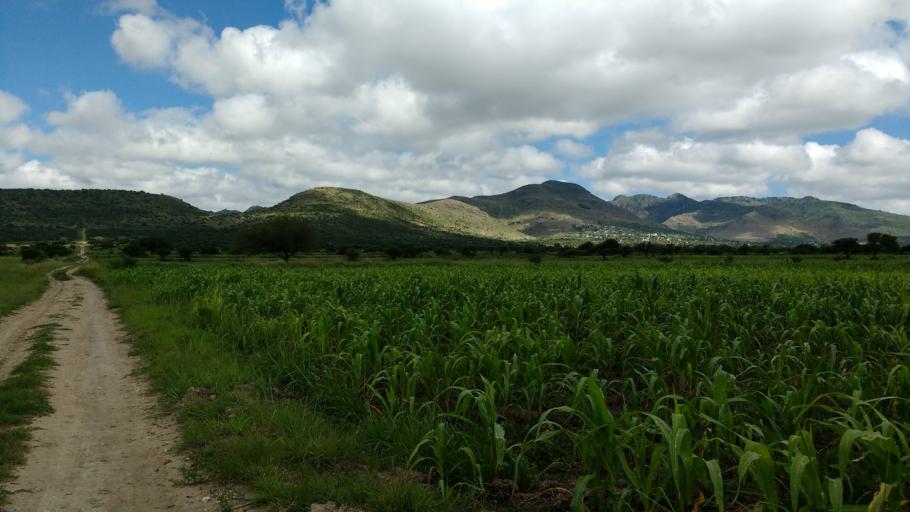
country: MX
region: Hidalgo
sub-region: Tezontepec de Aldama
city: Tenango
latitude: 20.2469
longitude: -99.2620
